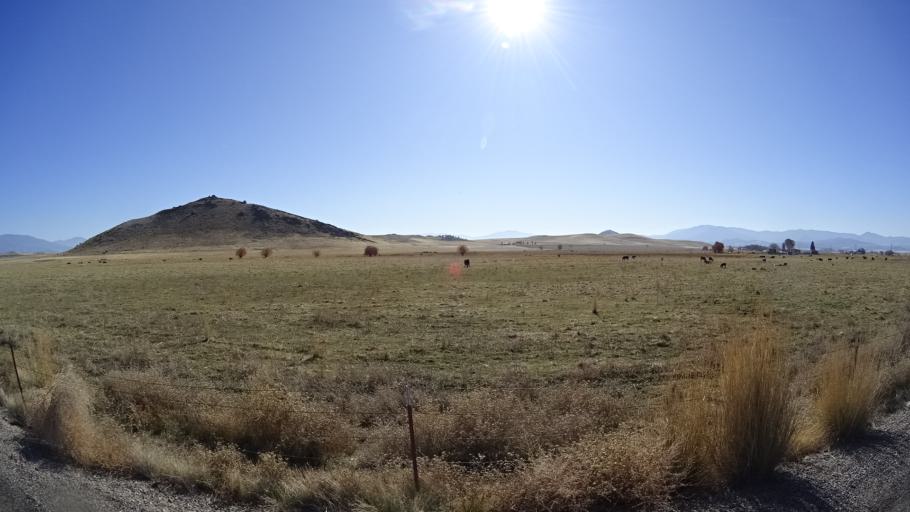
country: US
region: California
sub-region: Siskiyou County
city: Montague
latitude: 41.7567
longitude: -122.4926
